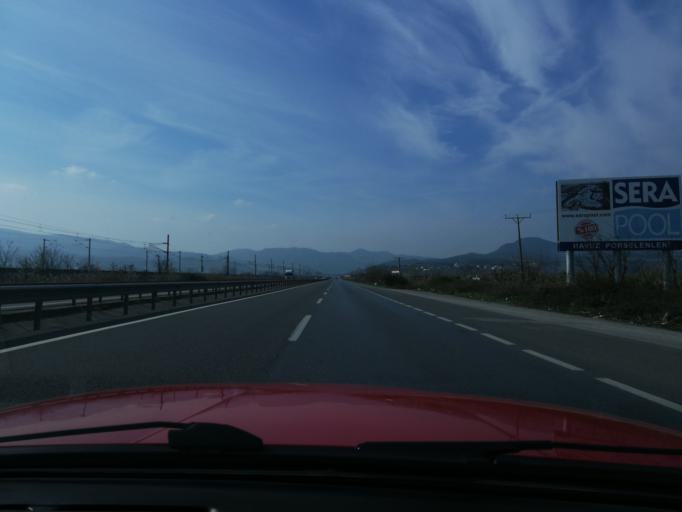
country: TR
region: Bilecik
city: Osmaneli
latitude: 40.4650
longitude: 30.0537
